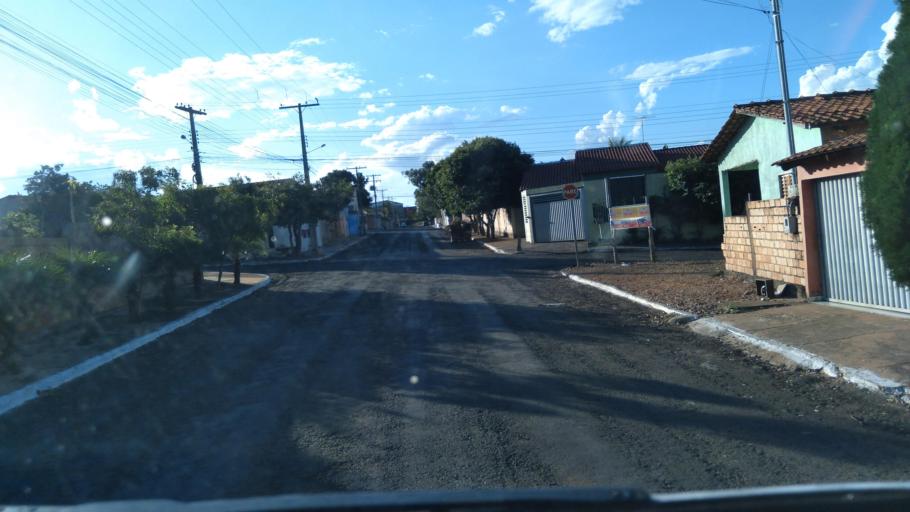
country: BR
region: Goias
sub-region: Mineiros
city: Mineiros
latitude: -17.5565
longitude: -52.5468
